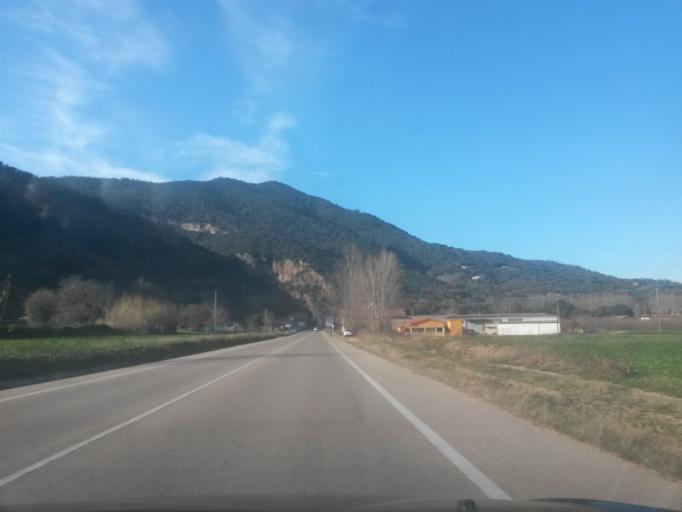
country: ES
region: Catalonia
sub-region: Provincia de Girona
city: la Cellera de Ter
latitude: 41.9816
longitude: 2.6093
